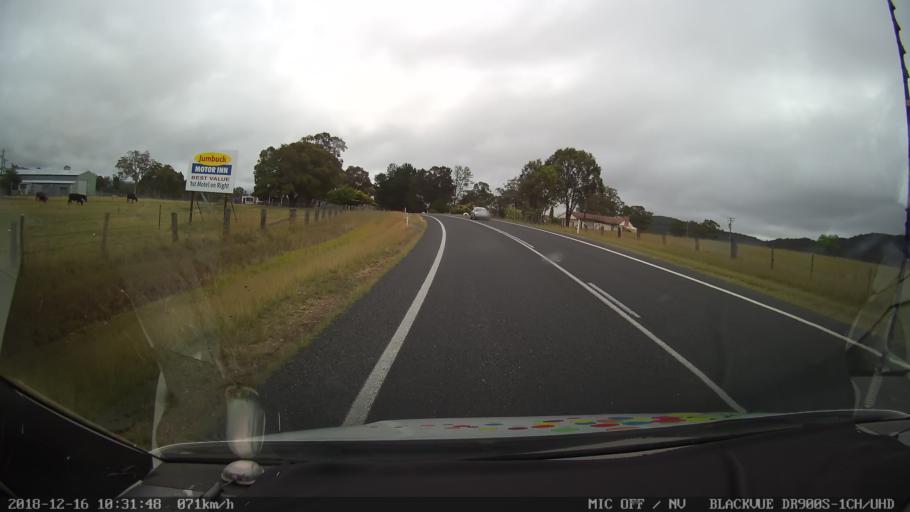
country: AU
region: New South Wales
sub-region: Tenterfield Municipality
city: Carrolls Creek
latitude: -29.0789
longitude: 152.0084
